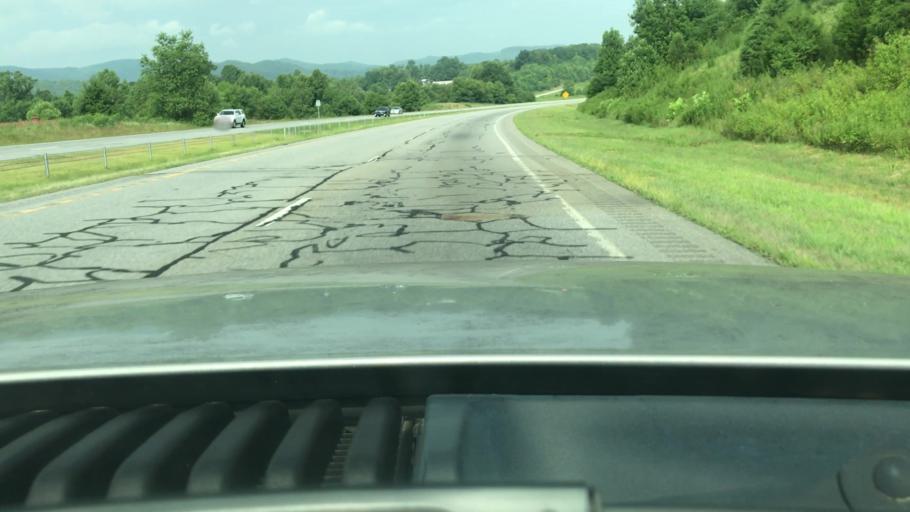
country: US
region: North Carolina
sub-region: Yadkin County
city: Jonesville
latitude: 36.1410
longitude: -80.8877
